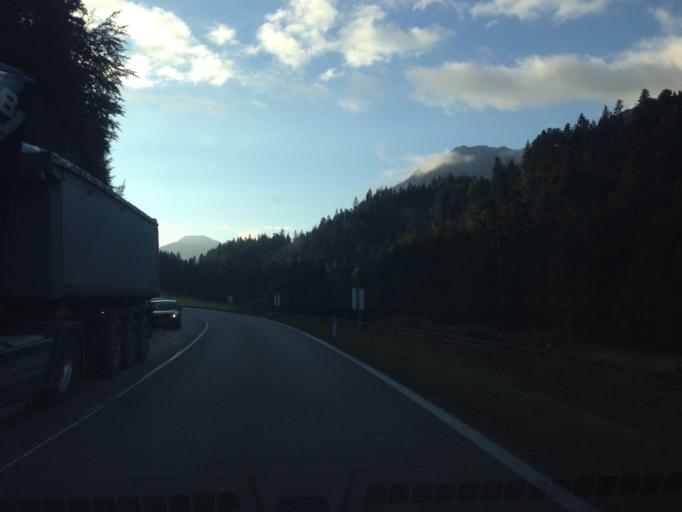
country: AT
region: Tyrol
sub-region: Politischer Bezirk Reutte
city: Ehenbichl
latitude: 47.4567
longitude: 10.7237
